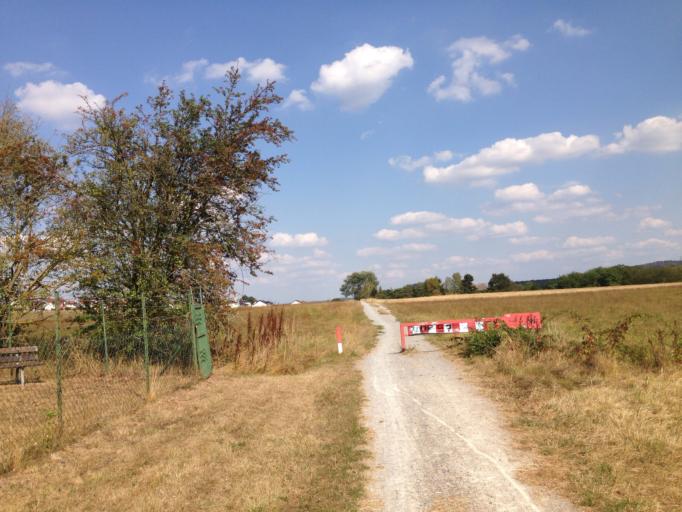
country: DE
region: Hesse
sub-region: Regierungsbezirk Giessen
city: Giessen
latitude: 50.6257
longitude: 8.6658
